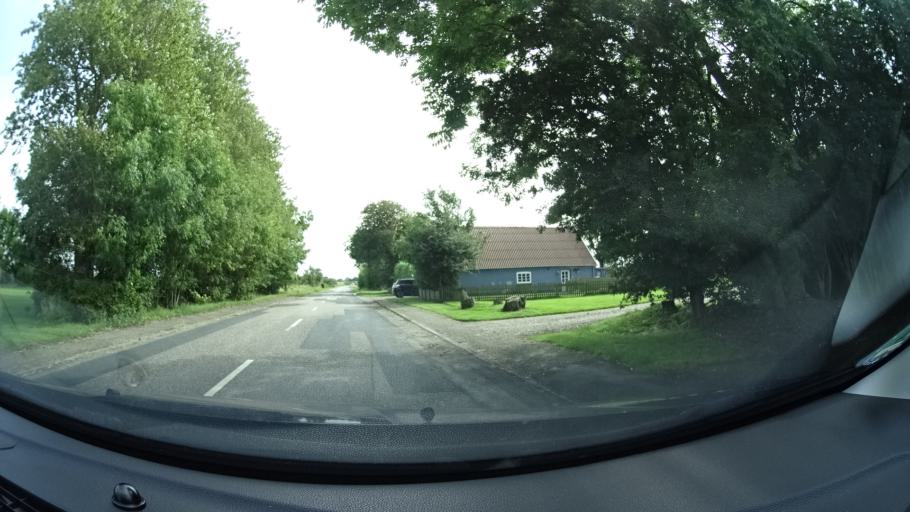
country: DK
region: South Denmark
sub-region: Tonder Kommune
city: Sherrebek
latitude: 55.0759
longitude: 8.6745
